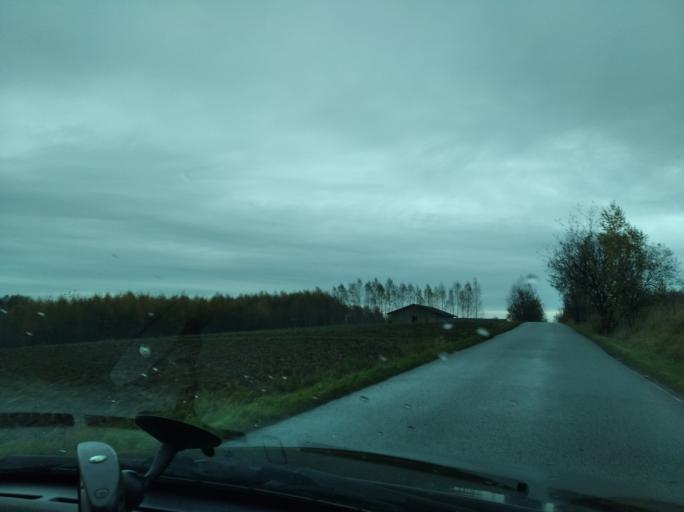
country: PL
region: Subcarpathian Voivodeship
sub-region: Powiat rzeszowski
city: Tyczyn
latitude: 49.9423
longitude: 22.0377
